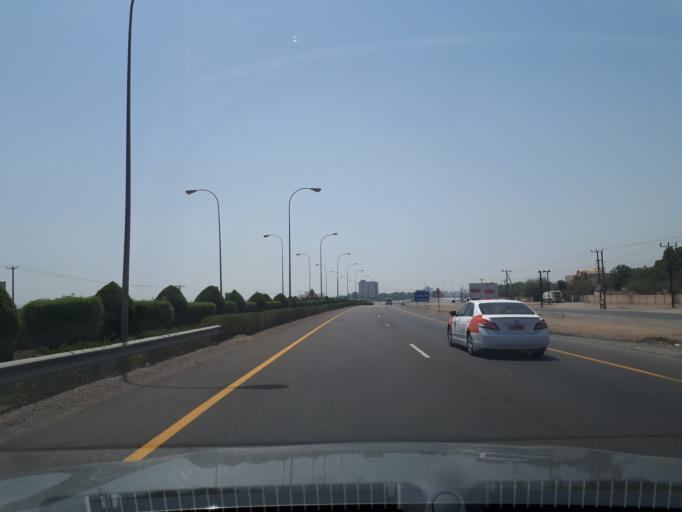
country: OM
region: Al Batinah
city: Al Sohar
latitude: 24.4124
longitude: 56.6354
